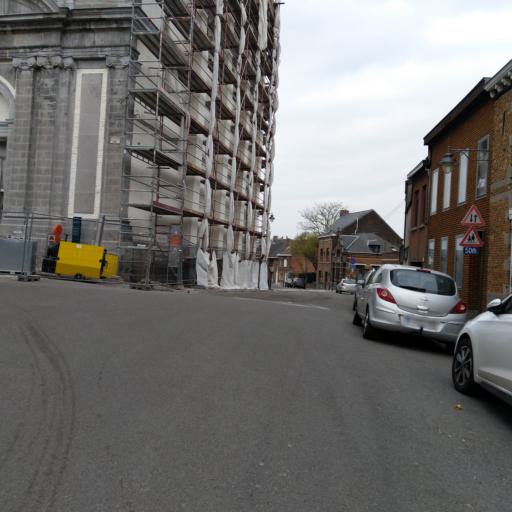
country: BE
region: Wallonia
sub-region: Province du Hainaut
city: Mons
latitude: 50.4582
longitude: 3.9534
